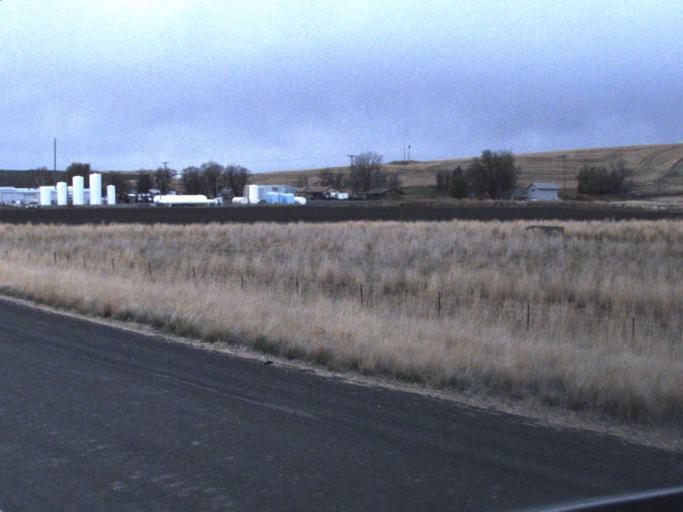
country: US
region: Washington
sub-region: Whitman County
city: Colfax
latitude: 46.8093
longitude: -117.6474
